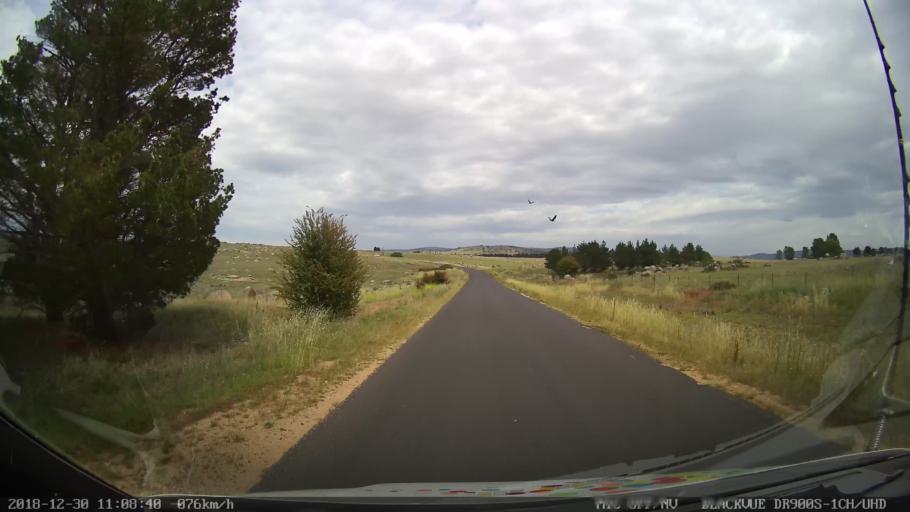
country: AU
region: New South Wales
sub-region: Snowy River
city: Berridale
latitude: -36.5039
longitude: 148.8037
